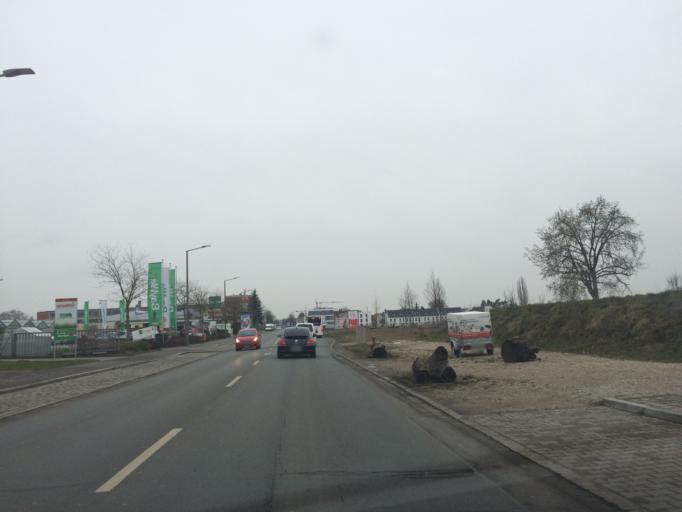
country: DE
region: Bavaria
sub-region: Regierungsbezirk Mittelfranken
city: Nuernberg
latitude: 49.4739
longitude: 11.0794
